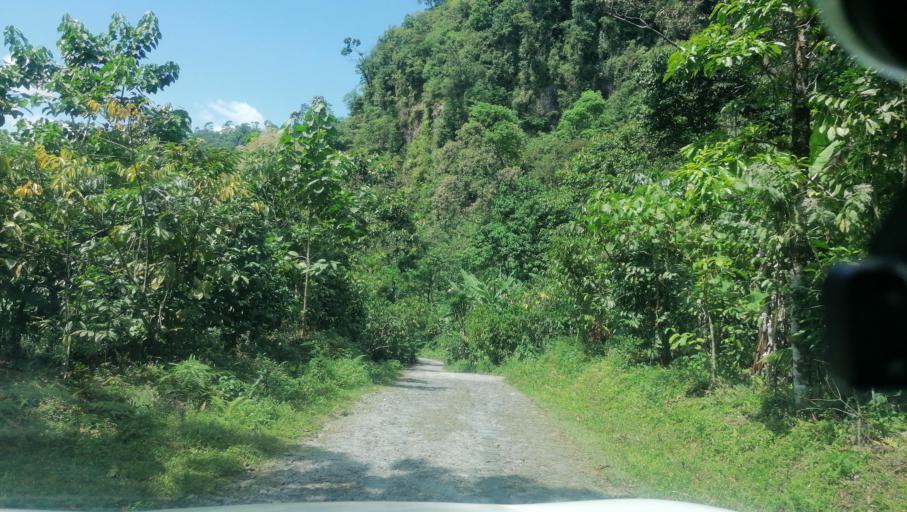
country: MX
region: Chiapas
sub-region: Union Juarez
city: Santo Domingo
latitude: 15.0719
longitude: -92.1305
